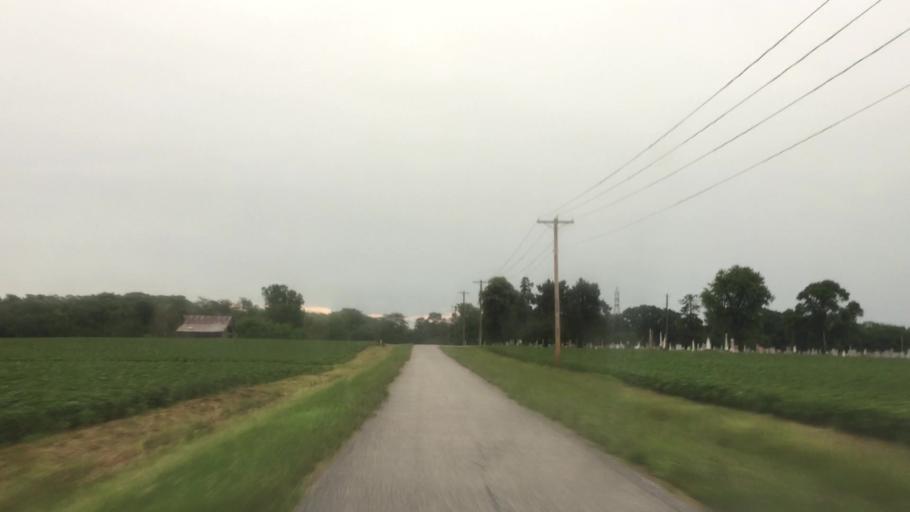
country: US
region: Illinois
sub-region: Hancock County
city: Nauvoo
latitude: 40.5494
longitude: -91.3560
